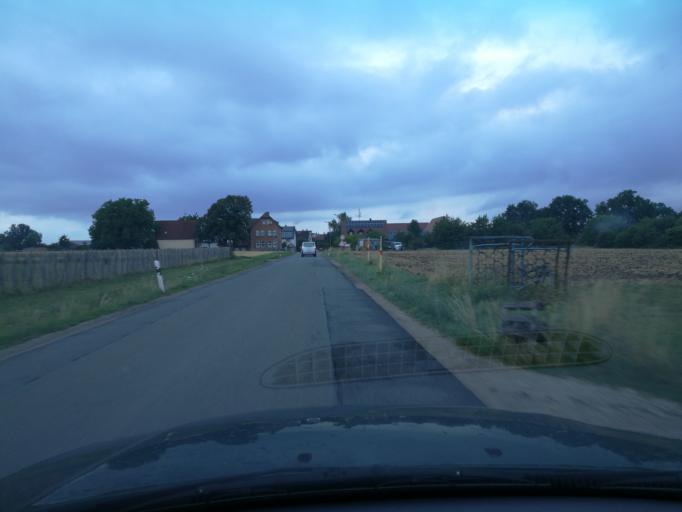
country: DE
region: Bavaria
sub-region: Regierungsbezirk Mittelfranken
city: Obermichelbach
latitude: 49.5370
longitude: 10.9597
